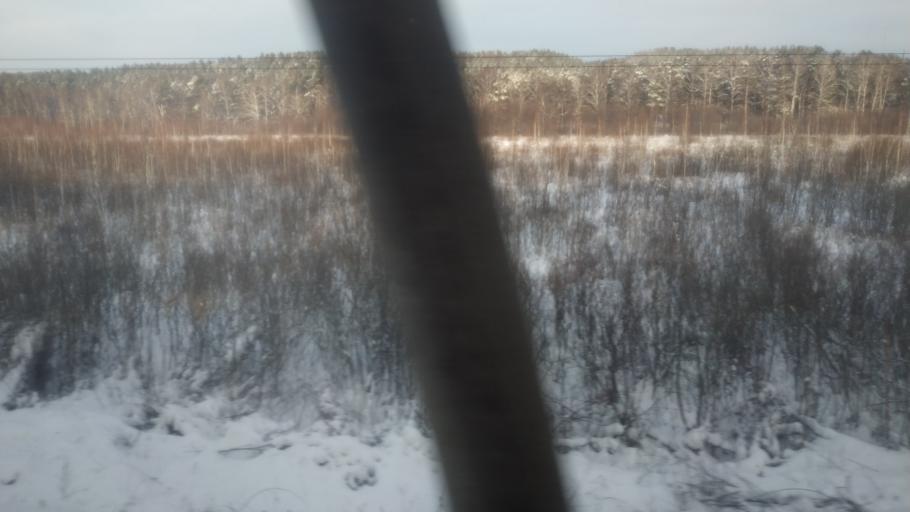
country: RU
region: Kirov
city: Krasnaya Polyana
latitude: 56.2535
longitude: 51.1371
